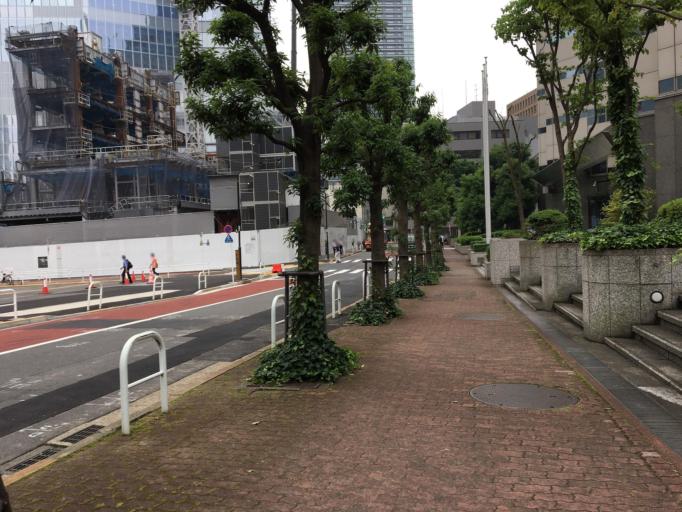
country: JP
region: Tokyo
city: Tokyo
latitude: 35.6679
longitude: 139.7446
